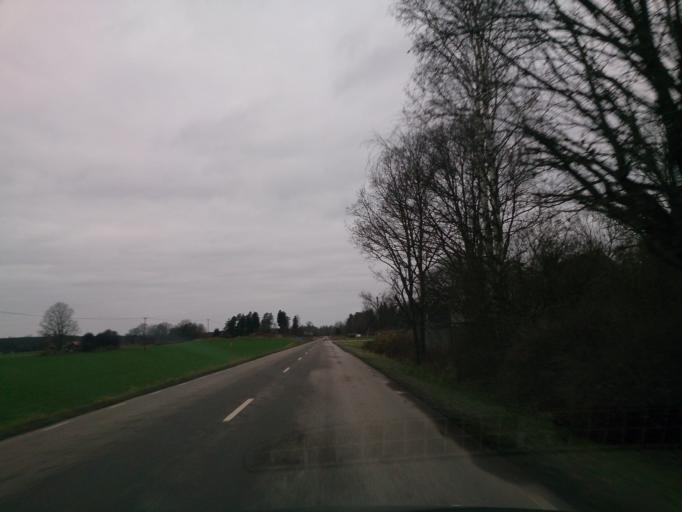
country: SE
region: OEstergoetland
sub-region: Norrkopings Kommun
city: Kimstad
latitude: 58.4106
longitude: 15.9244
